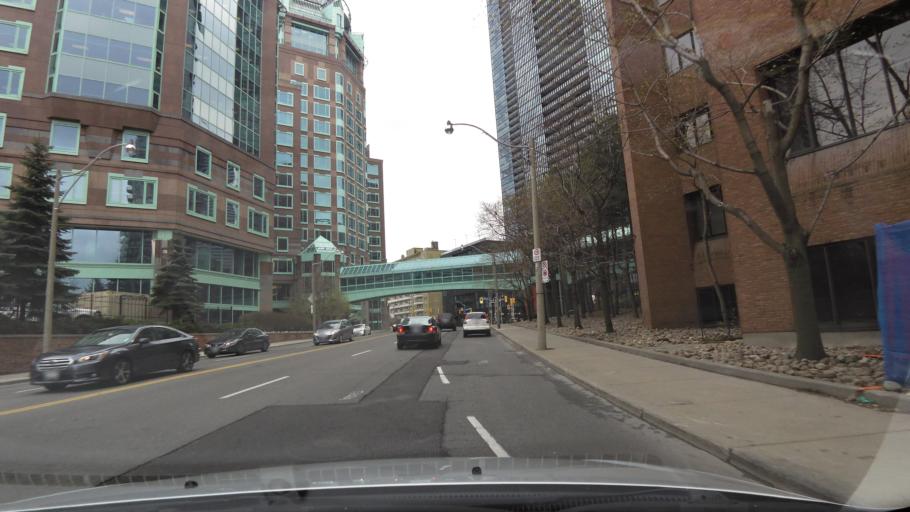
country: CA
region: Ontario
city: Toronto
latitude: 43.6711
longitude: -79.3795
